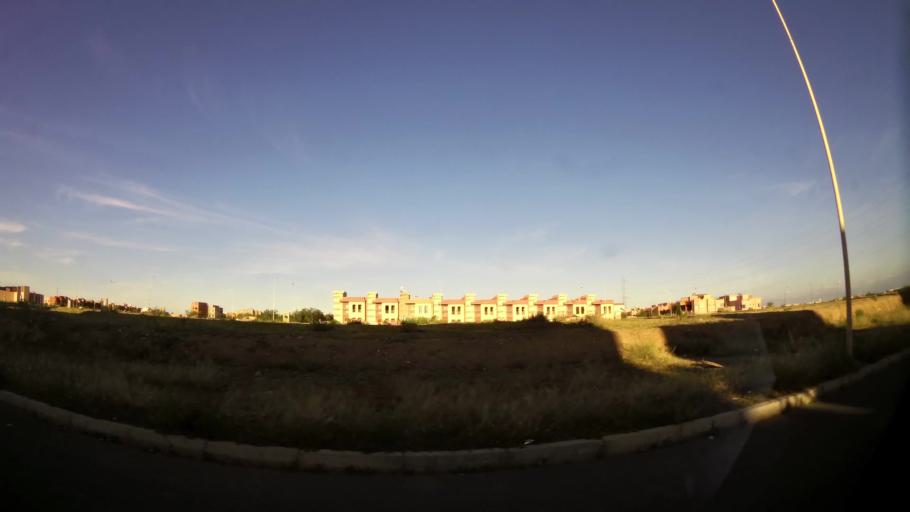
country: MA
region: Marrakech-Tensift-Al Haouz
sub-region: Marrakech
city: Marrakesh
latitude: 31.7439
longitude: -8.1150
